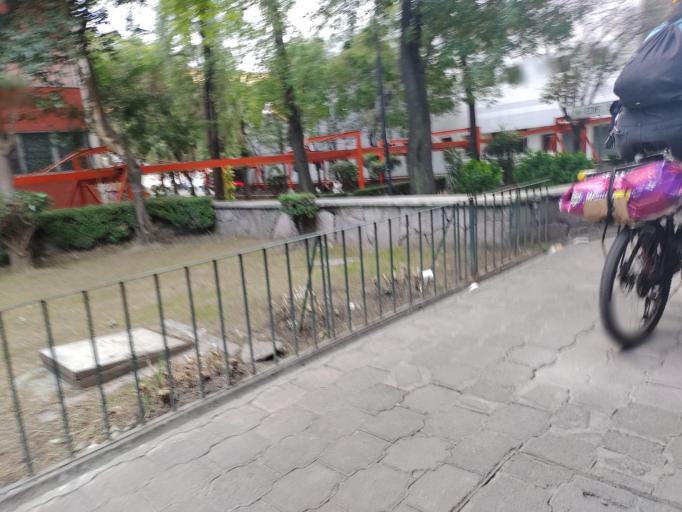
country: MX
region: Mexico City
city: Cuauhtemoc
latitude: 19.4551
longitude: -99.1467
